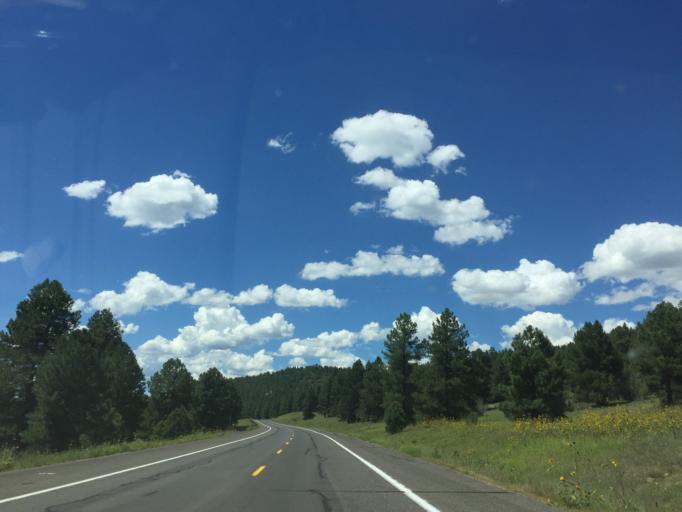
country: US
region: Arizona
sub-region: Coconino County
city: Mountainaire
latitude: 35.0899
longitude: -111.5362
